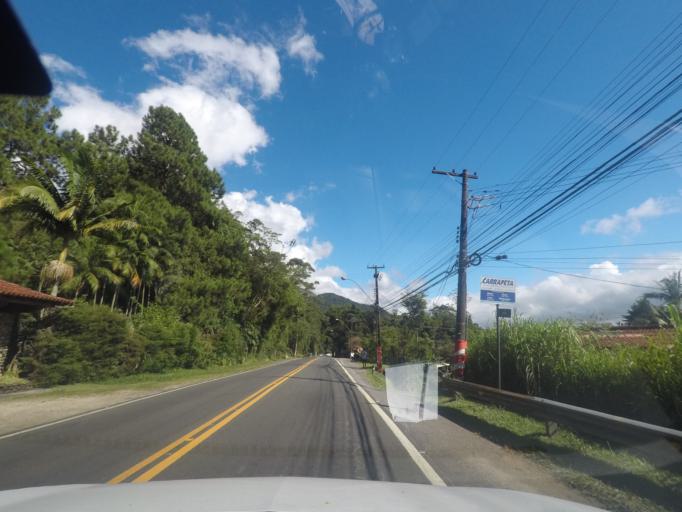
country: BR
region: Rio de Janeiro
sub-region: Teresopolis
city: Teresopolis
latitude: -22.4501
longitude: -42.9826
